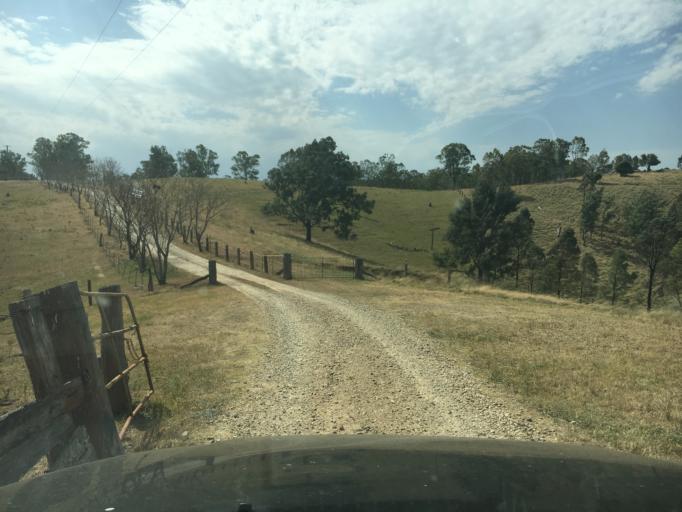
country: AU
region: New South Wales
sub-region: Cessnock
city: Branxton
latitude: -32.5005
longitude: 151.3168
